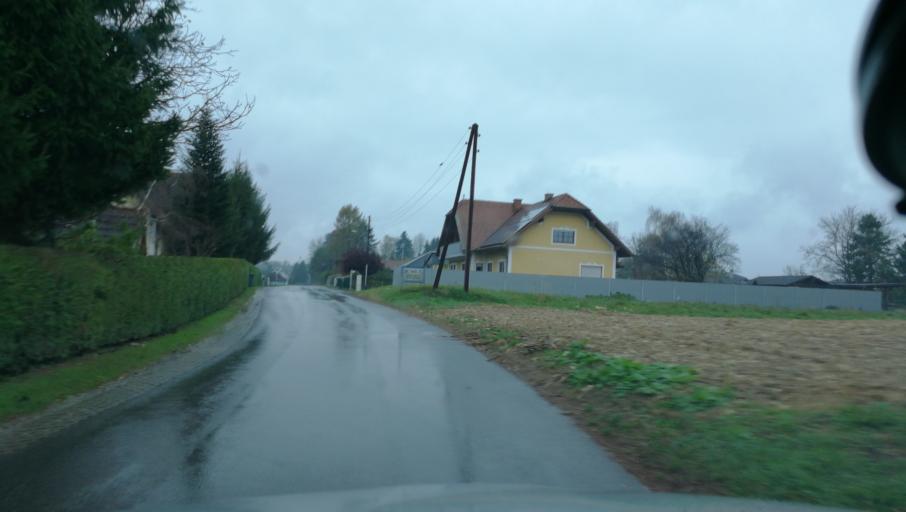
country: AT
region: Styria
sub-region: Politischer Bezirk Leibnitz
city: Strass in Steiermark
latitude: 46.7449
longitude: 15.6334
